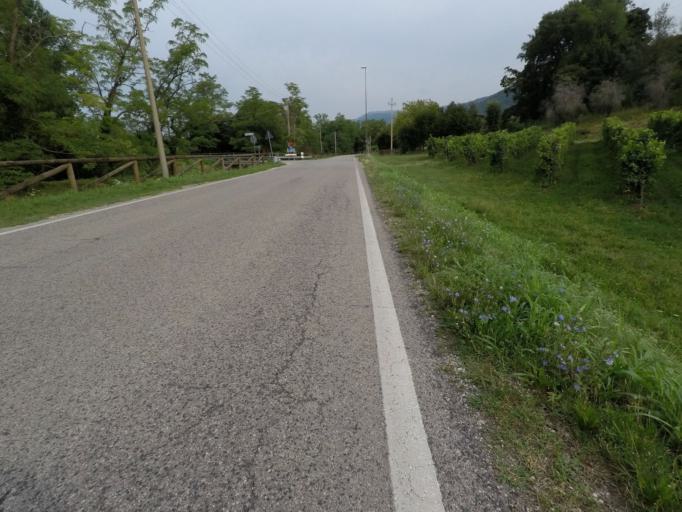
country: IT
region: Veneto
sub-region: Provincia di Treviso
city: Cordignano
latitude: 45.9687
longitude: 12.4130
